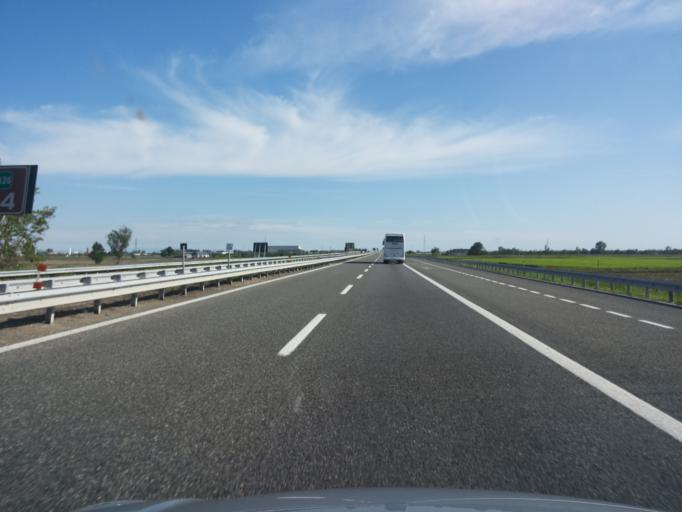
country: IT
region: Piedmont
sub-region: Provincia di Novara
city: Vicolungo
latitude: 45.4814
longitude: 8.4447
